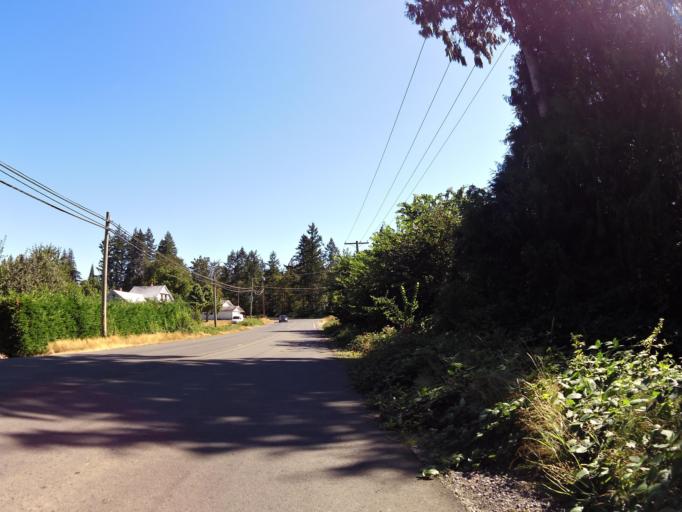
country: CA
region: British Columbia
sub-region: Cowichan Valley Regional District
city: Ladysmith
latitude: 48.9457
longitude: -123.7600
